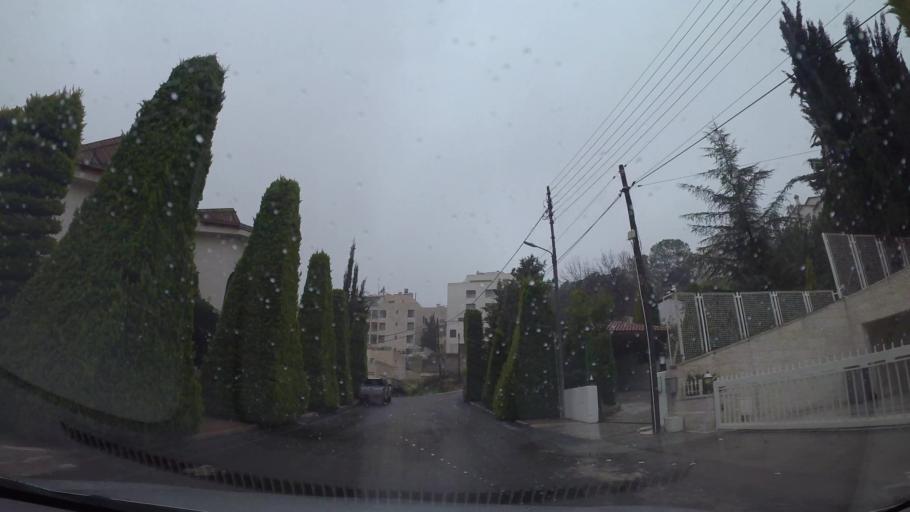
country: JO
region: Amman
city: Al Jubayhah
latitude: 32.0042
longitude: 35.8278
